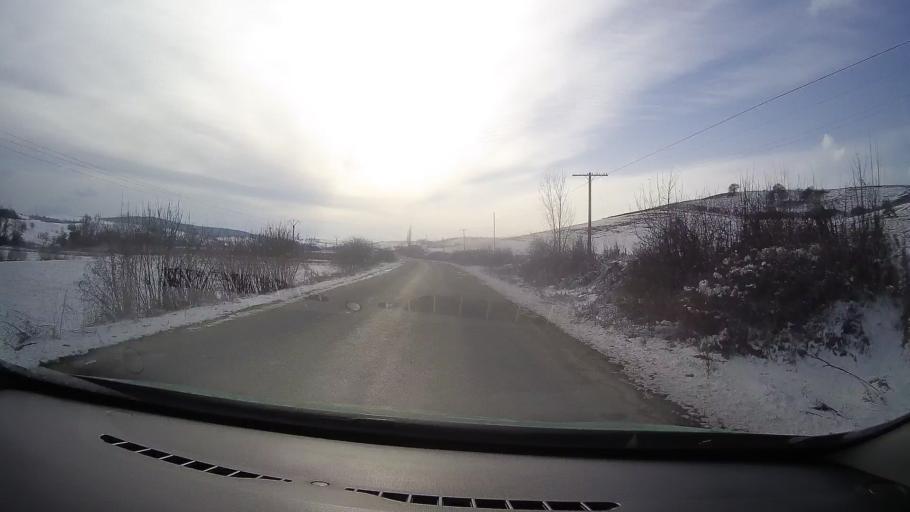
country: RO
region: Sibiu
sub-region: Oras Agnita
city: Ruja
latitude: 46.0143
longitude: 24.6897
